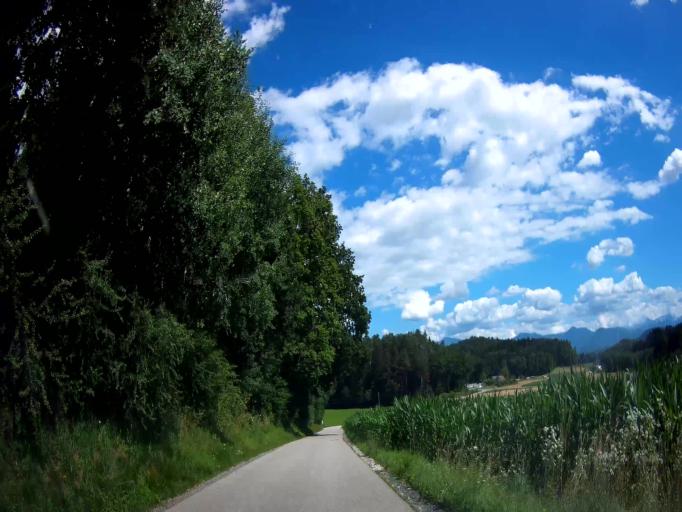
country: AT
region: Carinthia
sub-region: Politischer Bezirk Volkermarkt
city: Voelkermarkt
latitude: 46.6584
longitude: 14.5438
